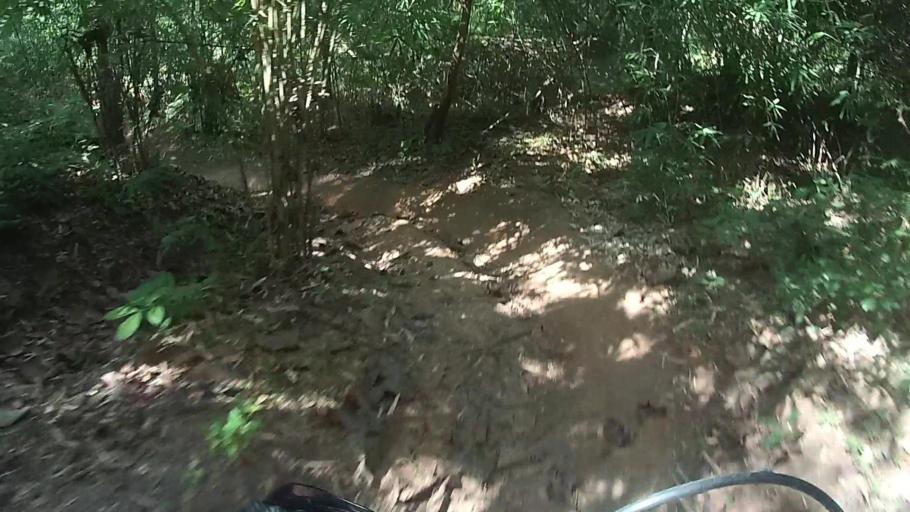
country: TH
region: Chiang Mai
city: San Sai
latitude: 18.9517
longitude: 99.0656
